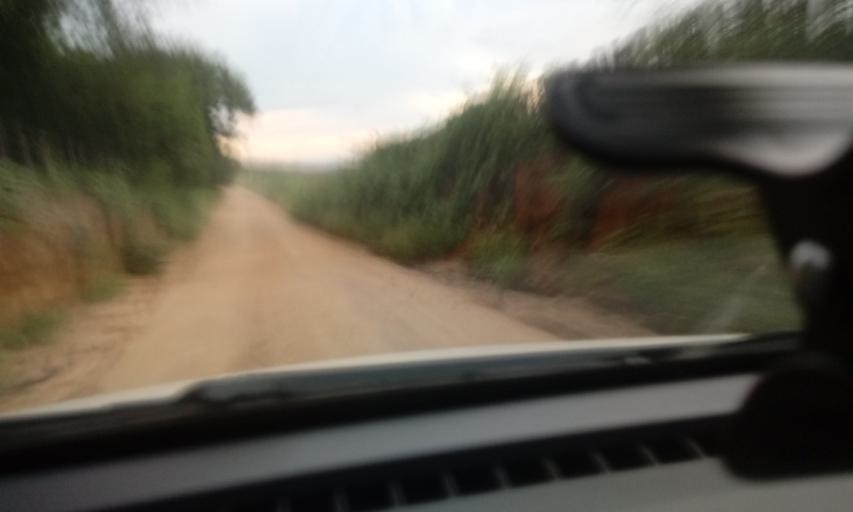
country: BR
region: Bahia
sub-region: Riacho De Santana
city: Riacho de Santana
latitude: -13.8093
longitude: -42.7582
